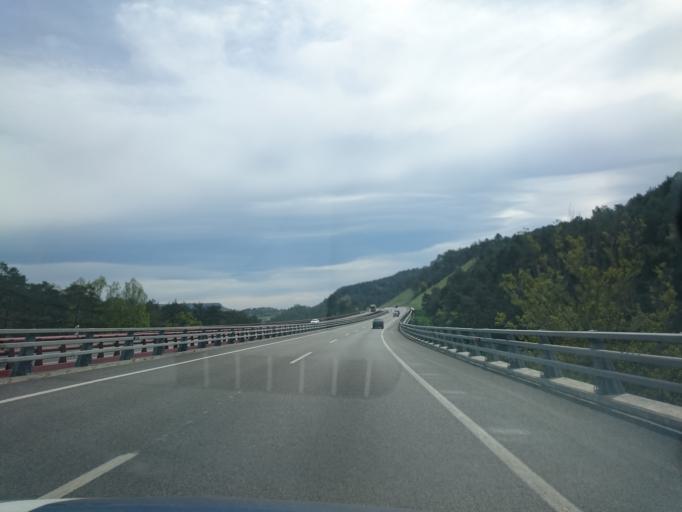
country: ES
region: Catalonia
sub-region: Provincia de Barcelona
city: Muntanyola
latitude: 41.9329
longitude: 2.1580
